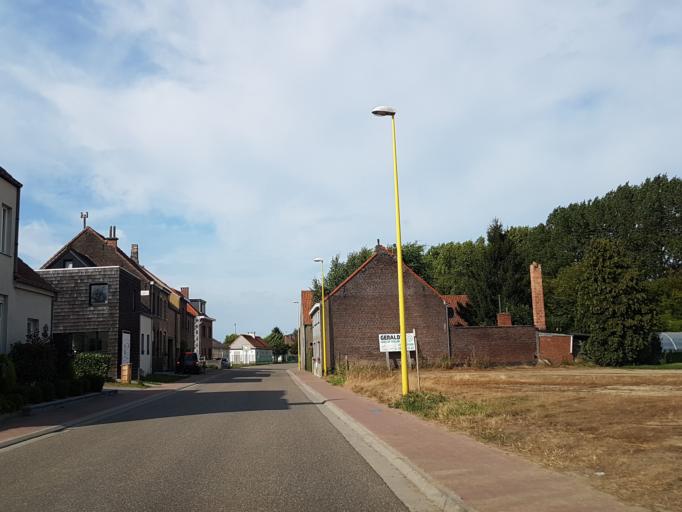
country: BE
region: Flanders
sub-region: Provincie Vlaams-Brabant
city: Grimbergen
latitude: 50.9471
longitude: 4.3965
